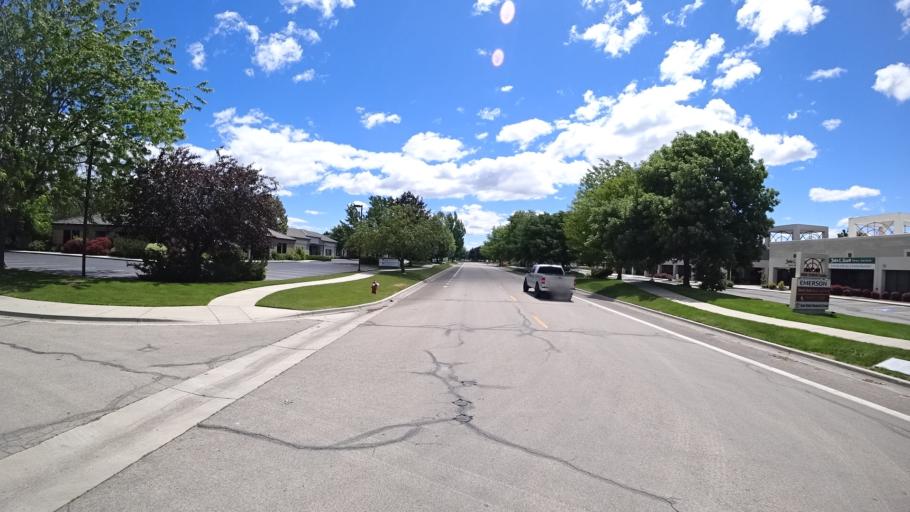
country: US
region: Idaho
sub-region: Ada County
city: Eagle
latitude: 43.6615
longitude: -116.3422
